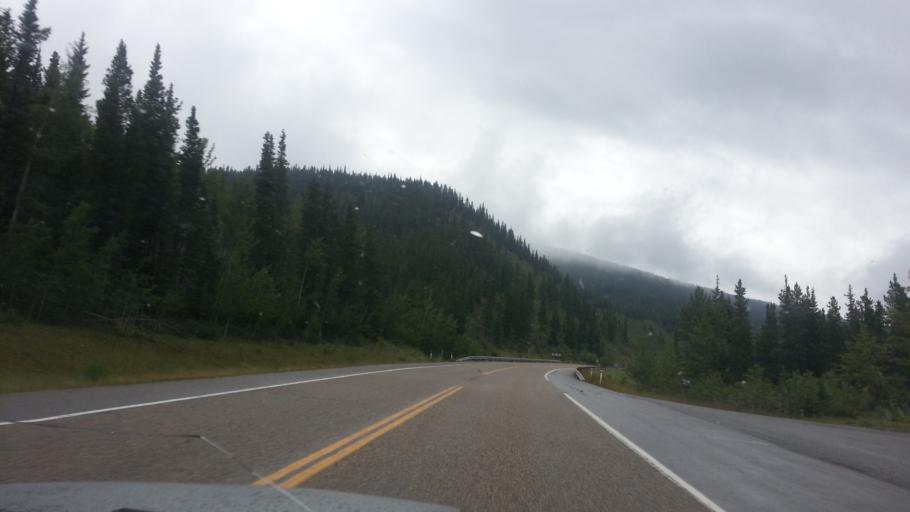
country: CA
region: Alberta
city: Cochrane
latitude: 50.8656
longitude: -114.7902
